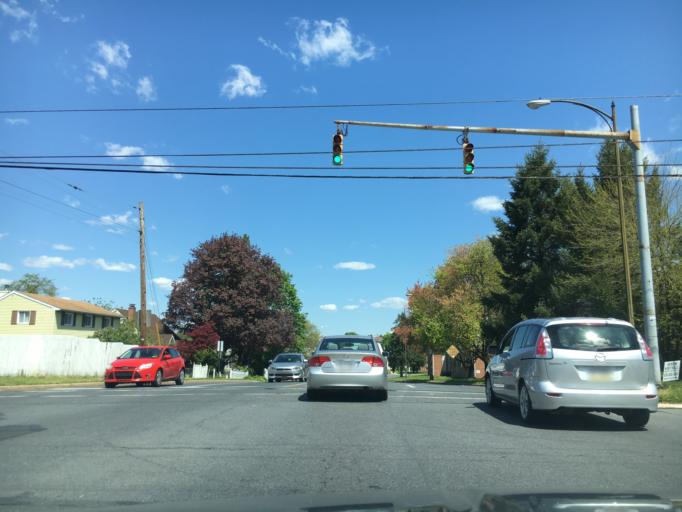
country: US
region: Pennsylvania
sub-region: Lehigh County
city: Allentown
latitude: 40.5885
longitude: -75.4793
